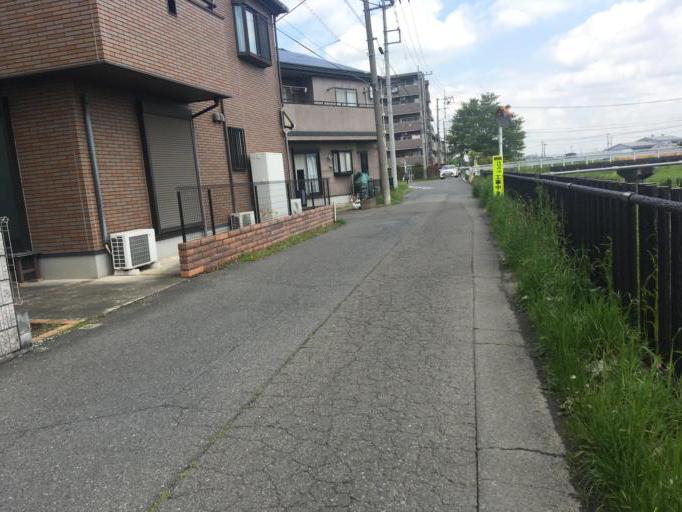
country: JP
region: Saitama
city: Kawagoe
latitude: 35.9046
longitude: 139.4938
